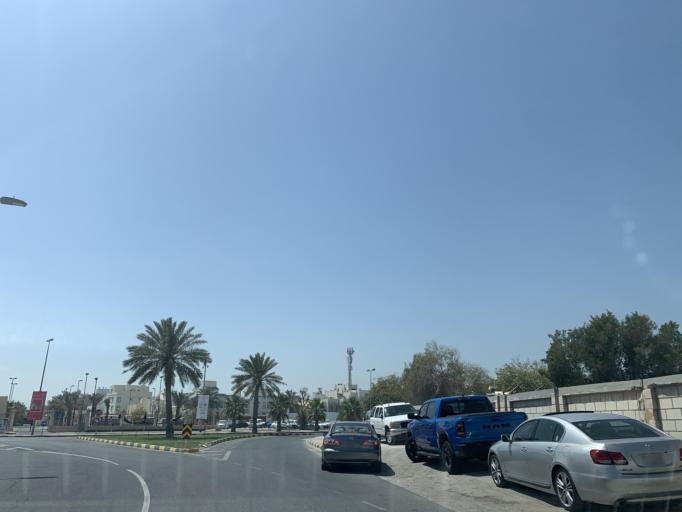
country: BH
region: Muharraq
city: Al Muharraq
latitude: 26.2683
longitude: 50.6190
